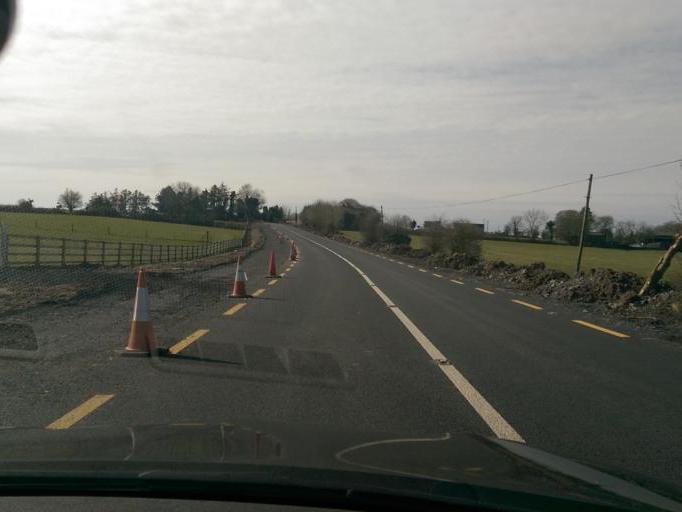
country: IE
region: Connaught
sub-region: County Galway
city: Athenry
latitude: 53.4801
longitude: -8.6060
